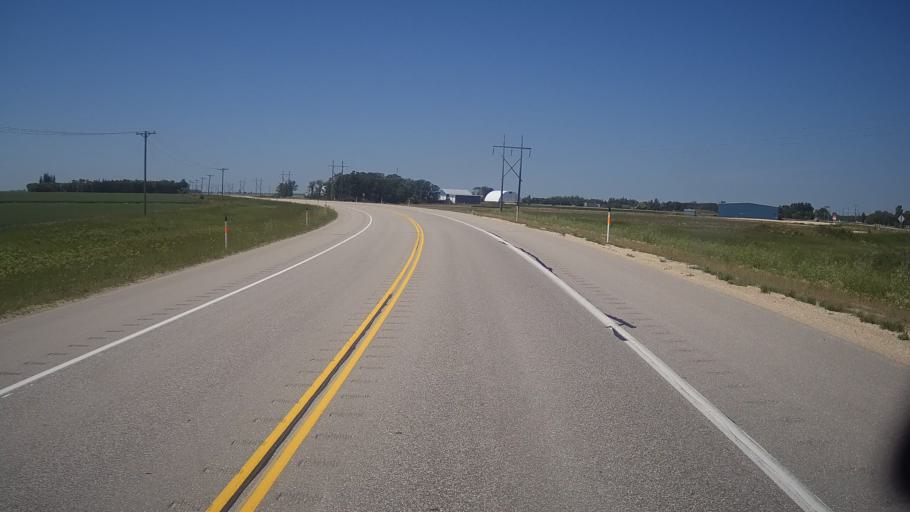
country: CA
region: Manitoba
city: Stonewall
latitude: 50.1225
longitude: -97.5328
